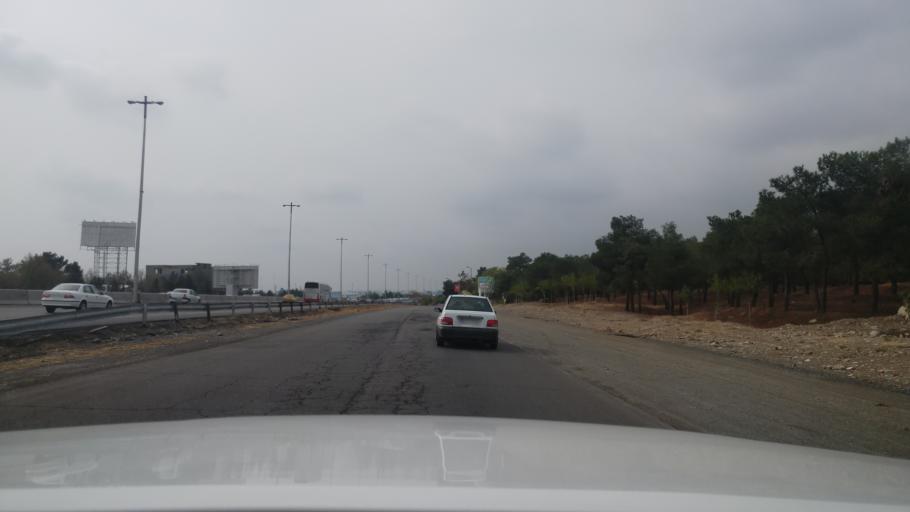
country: IR
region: Tehran
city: Shahr-e Qods
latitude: 35.7186
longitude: 51.2202
